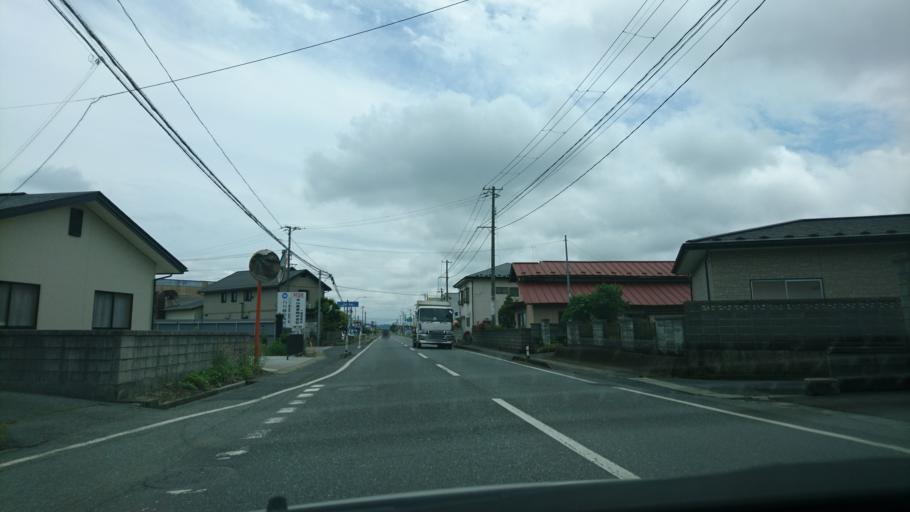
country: JP
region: Iwate
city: Ichinoseki
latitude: 38.9665
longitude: 141.1225
